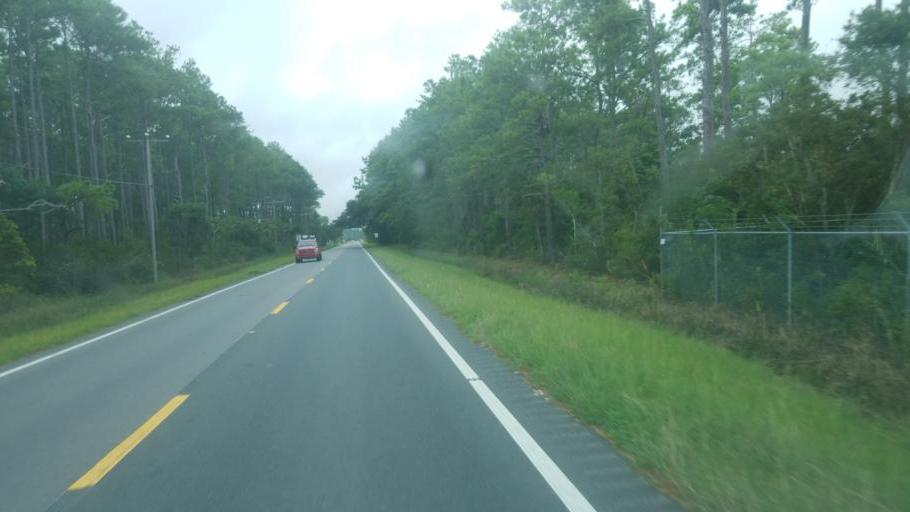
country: US
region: North Carolina
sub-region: Dare County
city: Wanchese
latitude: 35.8646
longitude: -75.6485
